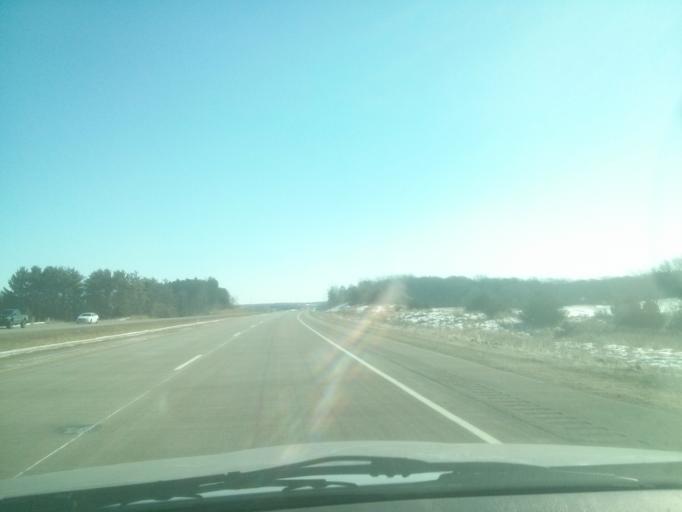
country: US
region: Wisconsin
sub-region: Saint Croix County
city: Somerset
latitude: 45.1079
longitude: -92.7084
